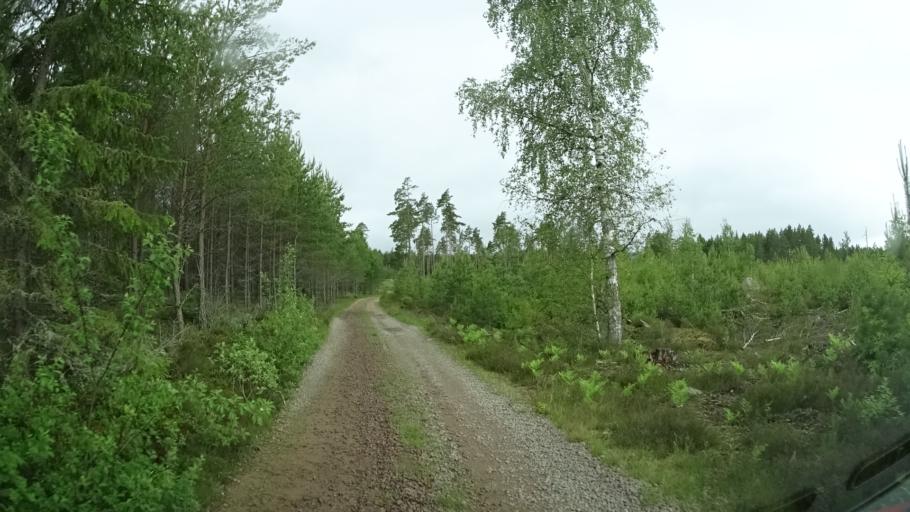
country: SE
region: Kalmar
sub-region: Vimmerby Kommun
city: Sodra Vi
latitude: 57.7151
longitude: 15.7811
